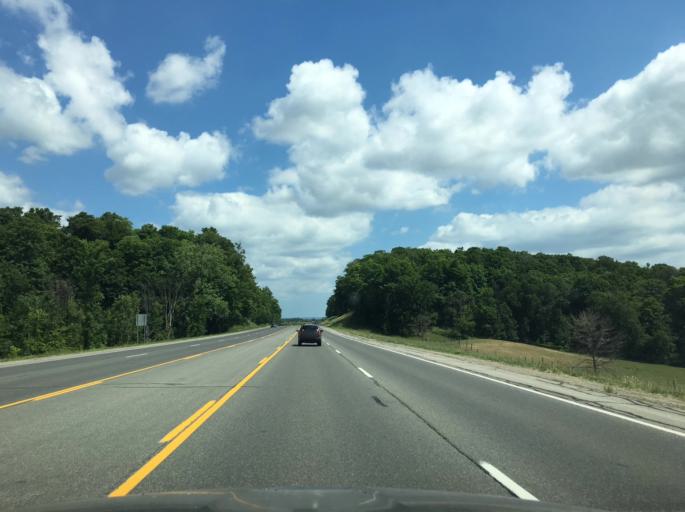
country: US
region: Michigan
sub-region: Grand Traverse County
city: Traverse City
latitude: 44.7101
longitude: -85.6507
